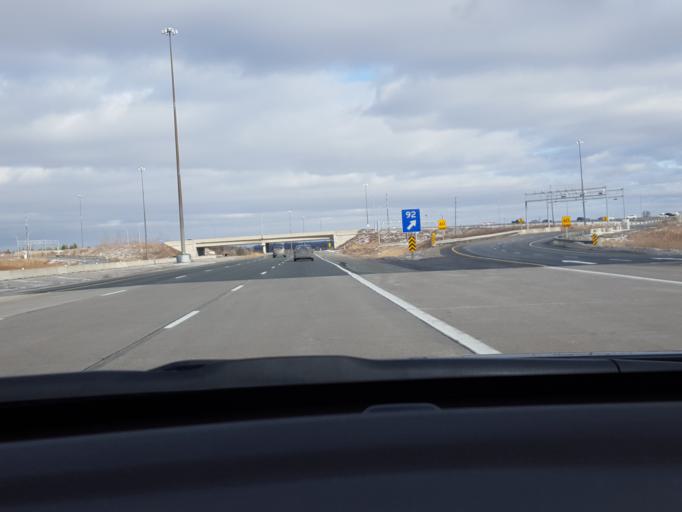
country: CA
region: Ontario
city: Markham
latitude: 43.8613
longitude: -79.2619
